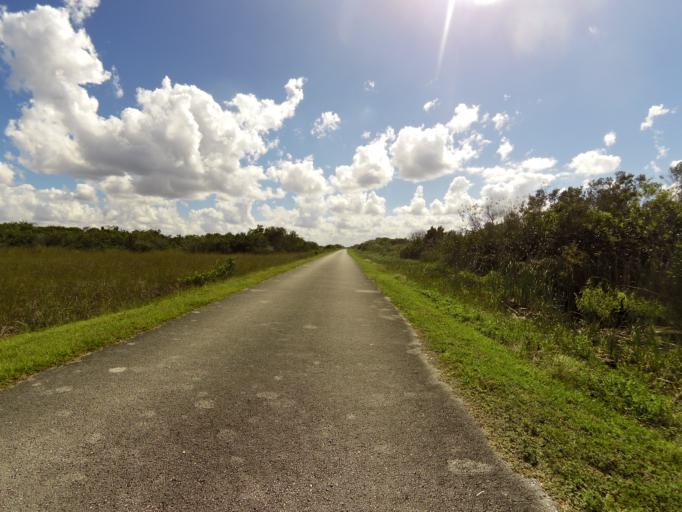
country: US
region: Florida
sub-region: Miami-Dade County
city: The Hammocks
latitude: 25.7082
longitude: -80.7668
